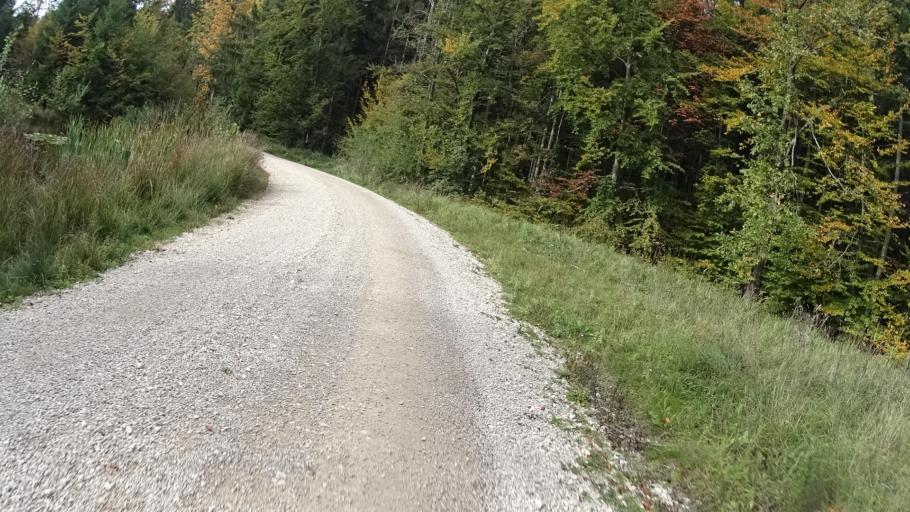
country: DE
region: Bavaria
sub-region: Upper Bavaria
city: Walting
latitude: 48.8971
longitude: 11.3315
